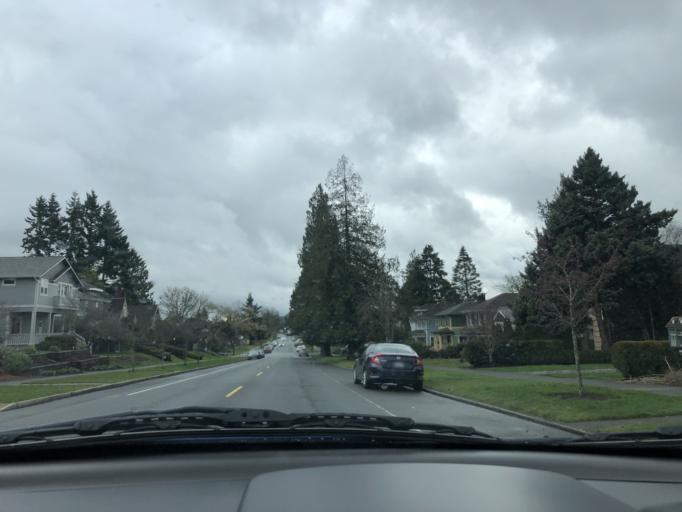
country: US
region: Washington
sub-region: Snohomish County
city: Everett
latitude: 48.0004
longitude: -122.2109
